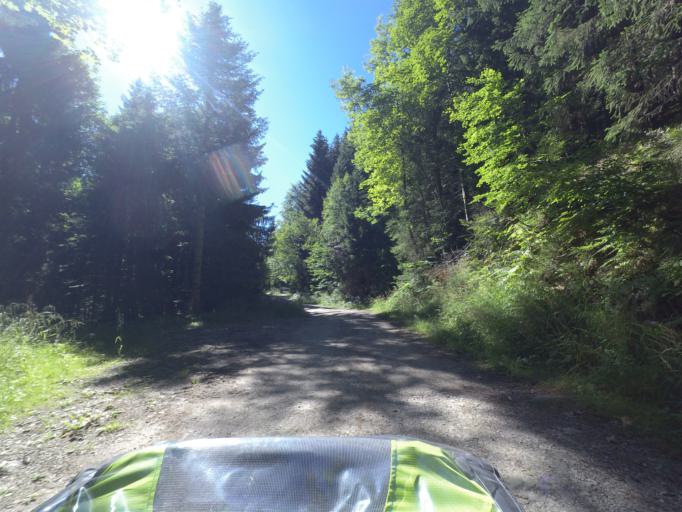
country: AT
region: Salzburg
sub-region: Politischer Bezirk Hallein
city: Hallein
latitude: 47.6418
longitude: 13.1000
